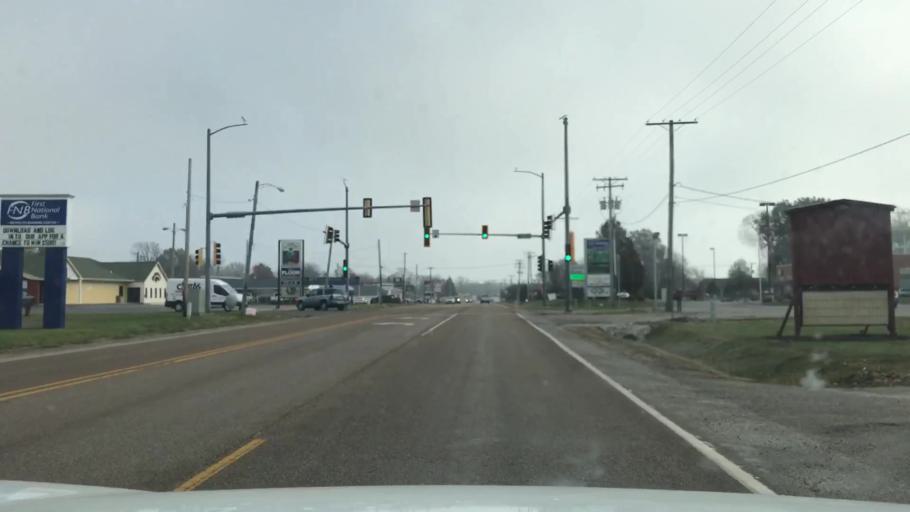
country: US
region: Illinois
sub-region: Madison County
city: Bethalto
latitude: 38.9010
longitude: -90.0475
